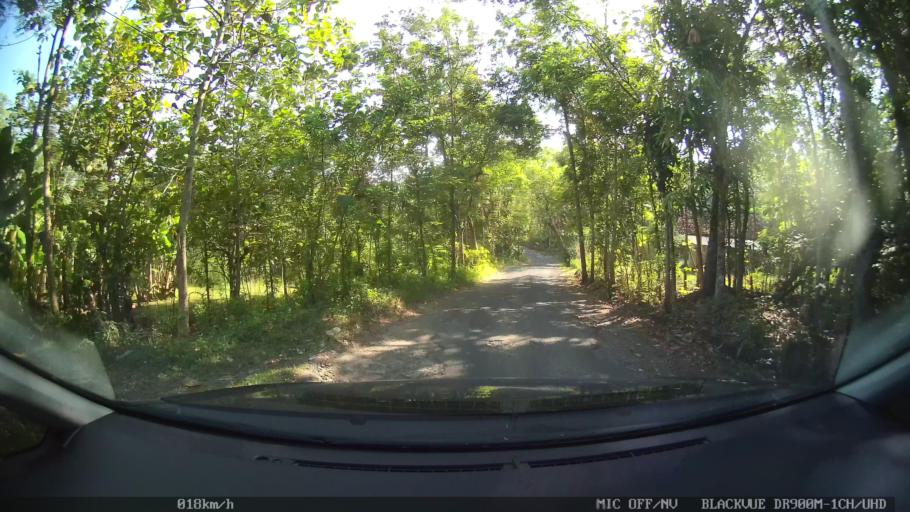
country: ID
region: Daerah Istimewa Yogyakarta
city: Kasihan
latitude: -7.8343
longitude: 110.2866
